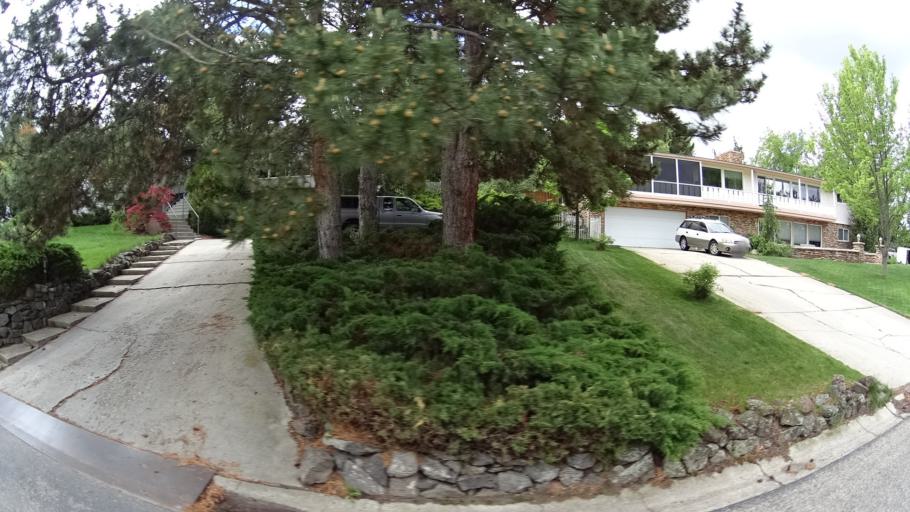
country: US
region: Idaho
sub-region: Ada County
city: Boise
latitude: 43.6473
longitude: -116.1840
